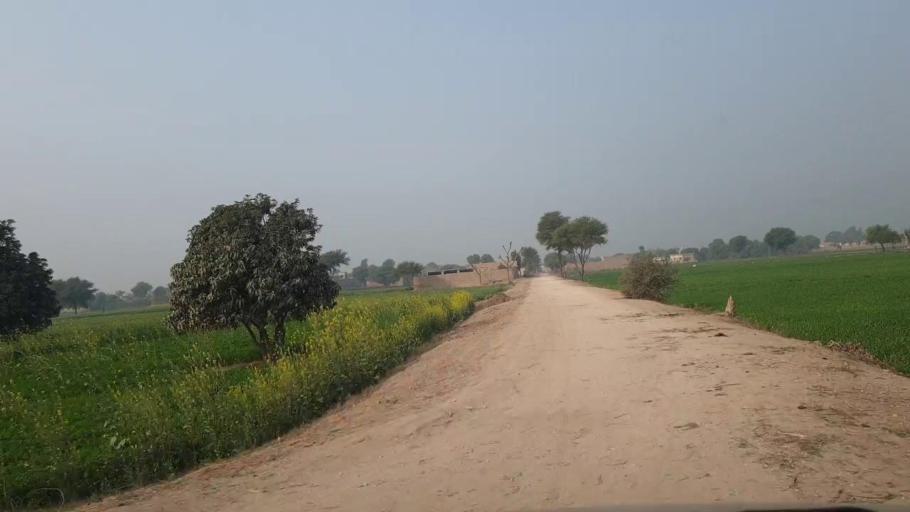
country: PK
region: Sindh
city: Hala
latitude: 25.8805
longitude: 68.3872
